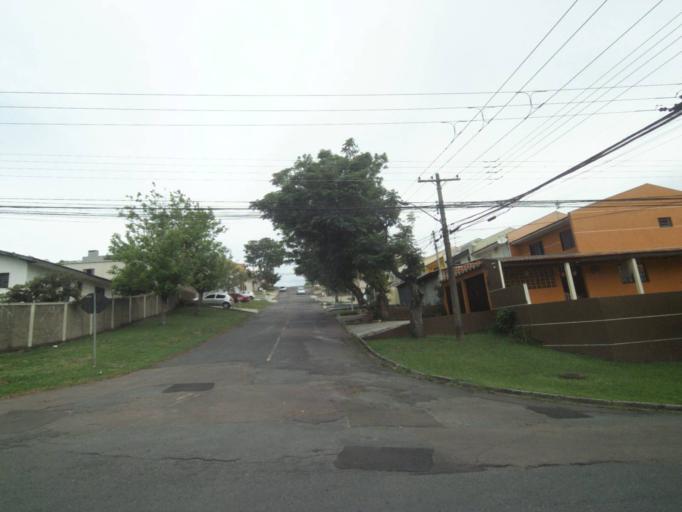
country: BR
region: Parana
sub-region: Pinhais
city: Pinhais
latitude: -25.4178
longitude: -49.2077
